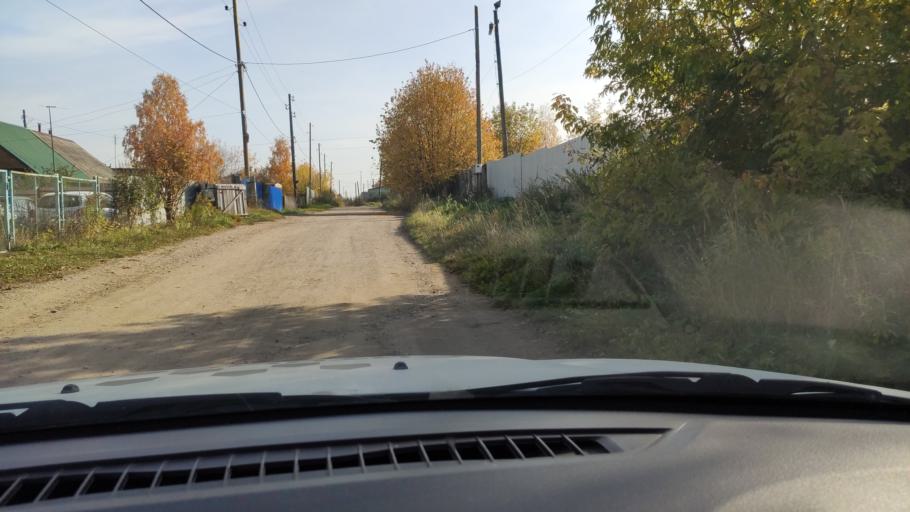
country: RU
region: Perm
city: Sylva
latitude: 58.0474
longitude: 56.7350
